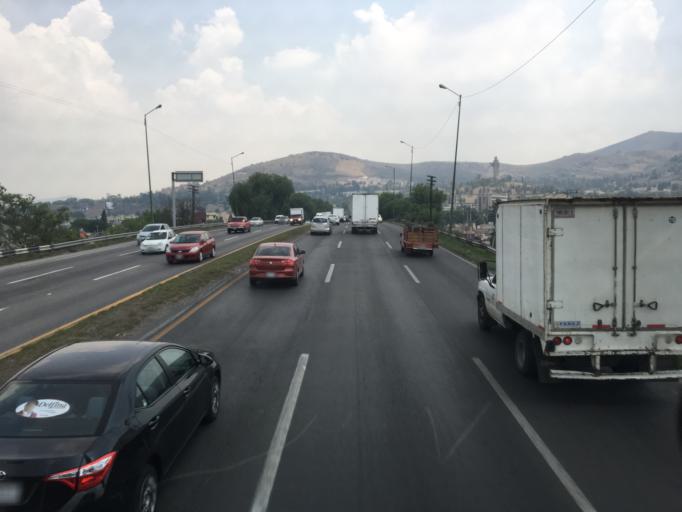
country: MX
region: Mexico
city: Tlalnepantla
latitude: 19.5534
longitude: -99.1847
